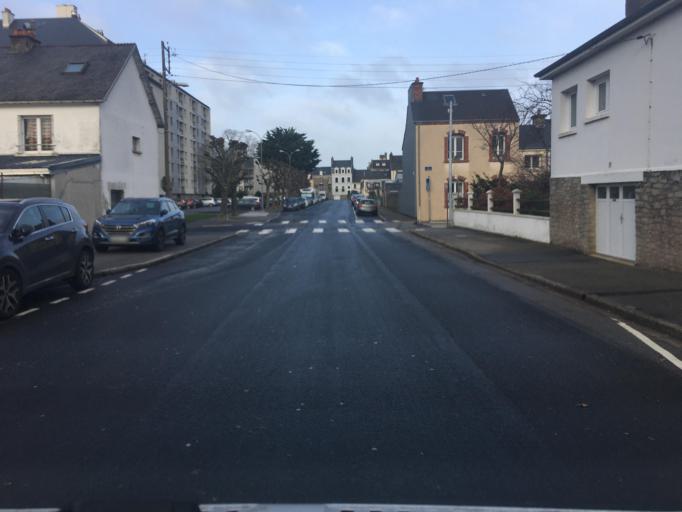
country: FR
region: Lower Normandy
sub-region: Departement de la Manche
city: Cherbourg-Octeville
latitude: 49.6373
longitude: -1.6055
